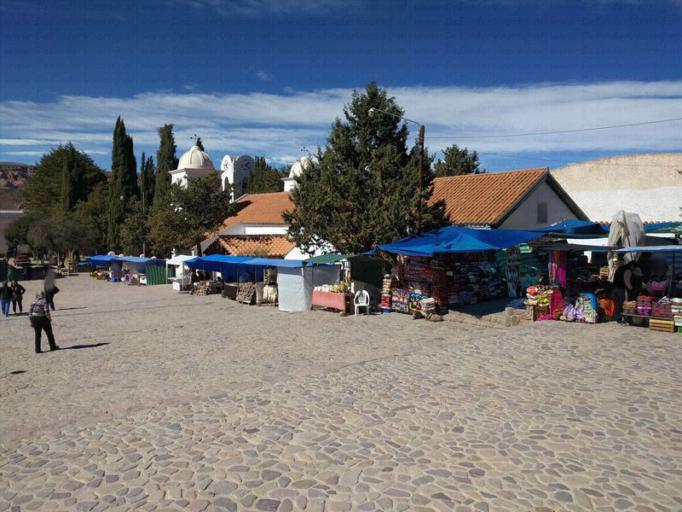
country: AR
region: Jujuy
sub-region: Departamento de Humahuaca
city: Humahuaca
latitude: -23.2039
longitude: -65.3495
